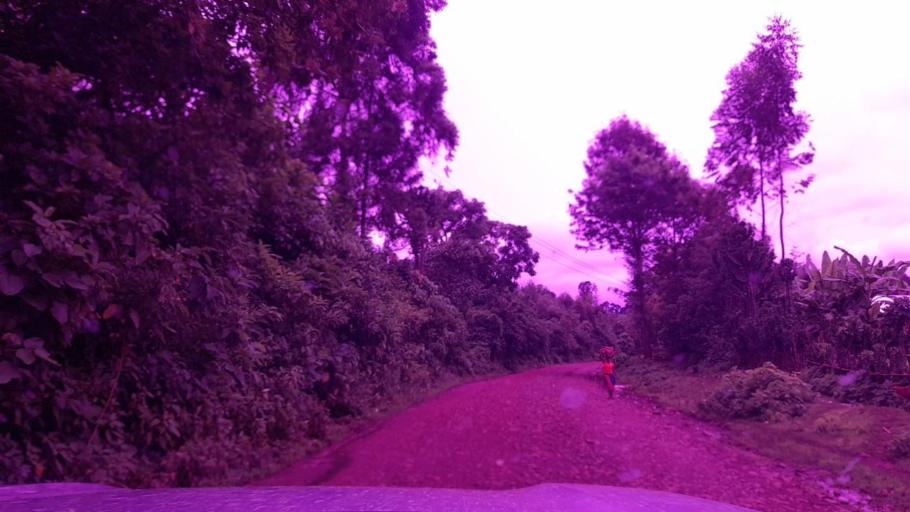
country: ET
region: Southern Nations, Nationalities, and People's Region
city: Tippi
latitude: 7.5848
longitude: 35.7712
